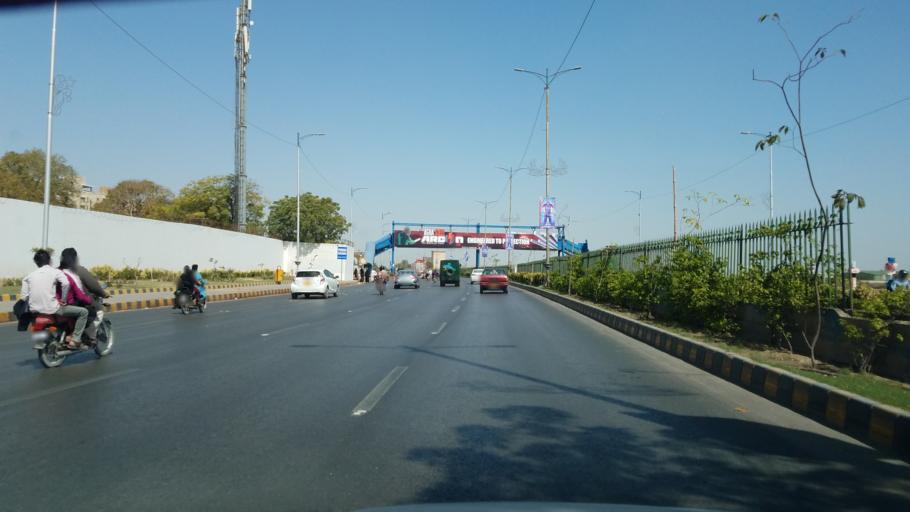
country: PK
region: Sindh
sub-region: Karachi District
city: Karachi
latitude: 24.8762
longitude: 67.0999
